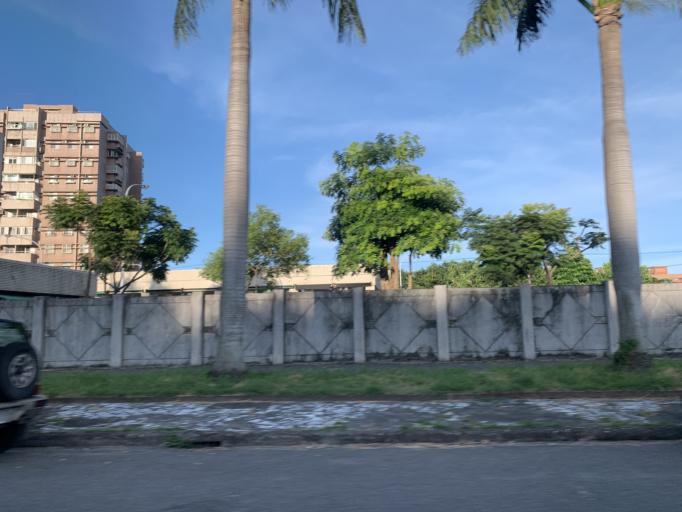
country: TW
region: Taiwan
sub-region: Hualien
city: Hualian
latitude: 24.0022
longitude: 121.6293
